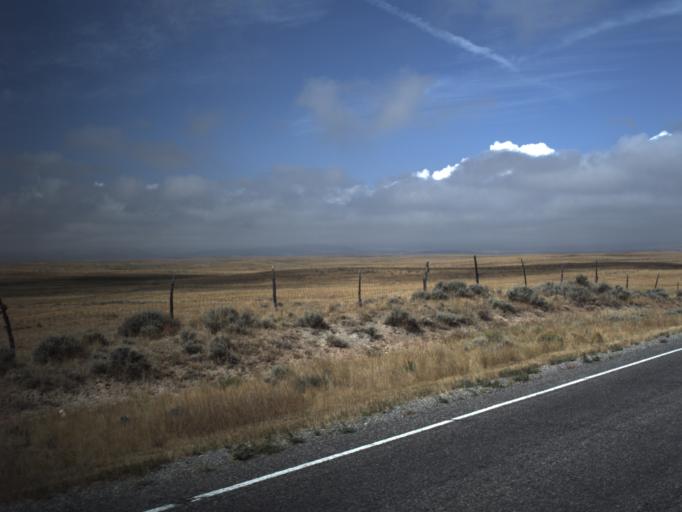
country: US
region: Wyoming
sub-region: Uinta County
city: Evanston
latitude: 41.4499
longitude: -111.0852
